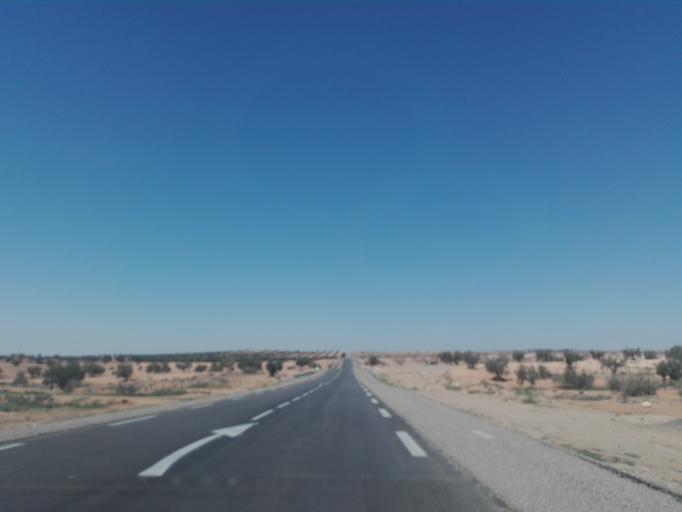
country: TN
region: Safaqis
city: Bi'r `Ali Bin Khalifah
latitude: 34.7585
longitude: 10.2944
